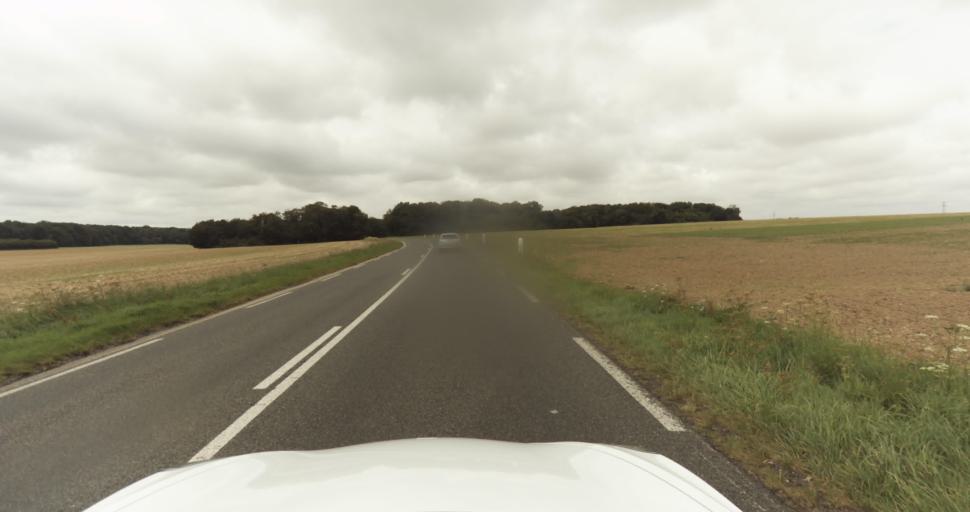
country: FR
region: Haute-Normandie
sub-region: Departement de l'Eure
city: Saint-Sebastien-de-Morsent
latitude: 49.0325
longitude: 1.0813
